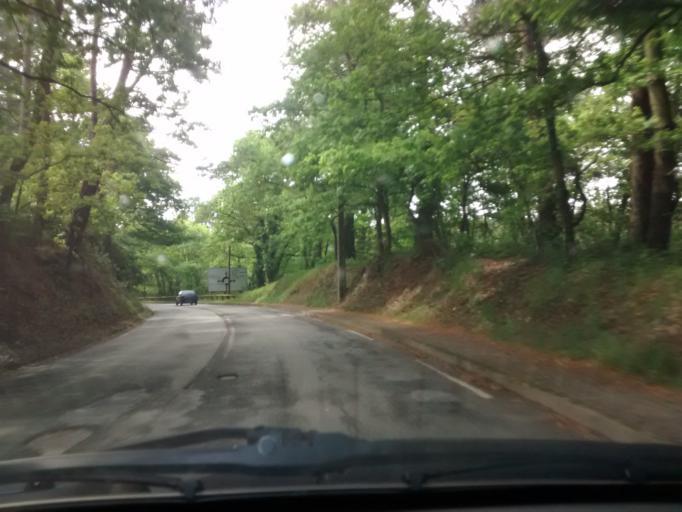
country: FR
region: Brittany
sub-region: Departement du Morbihan
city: Arradon
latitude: 47.6515
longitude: -2.7966
